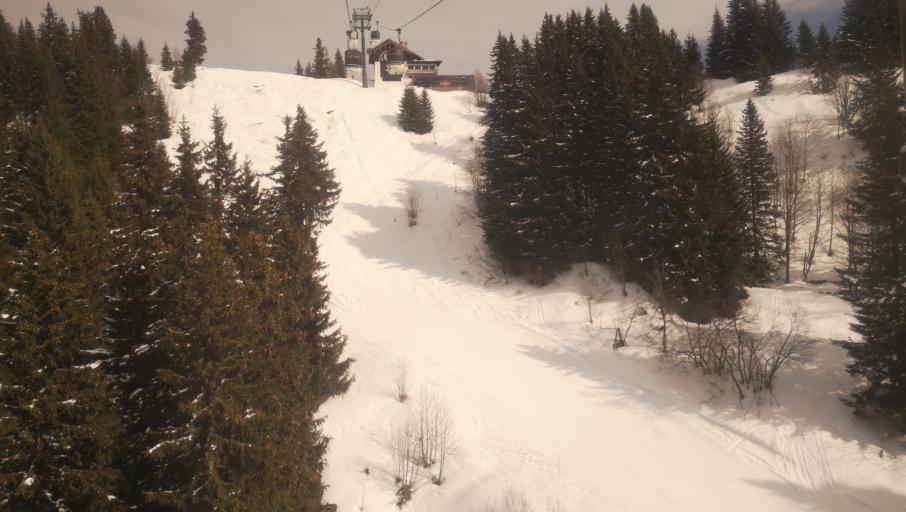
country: FR
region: Rhone-Alpes
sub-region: Departement de la Haute-Savoie
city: Megeve
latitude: 45.8571
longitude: 6.6534
